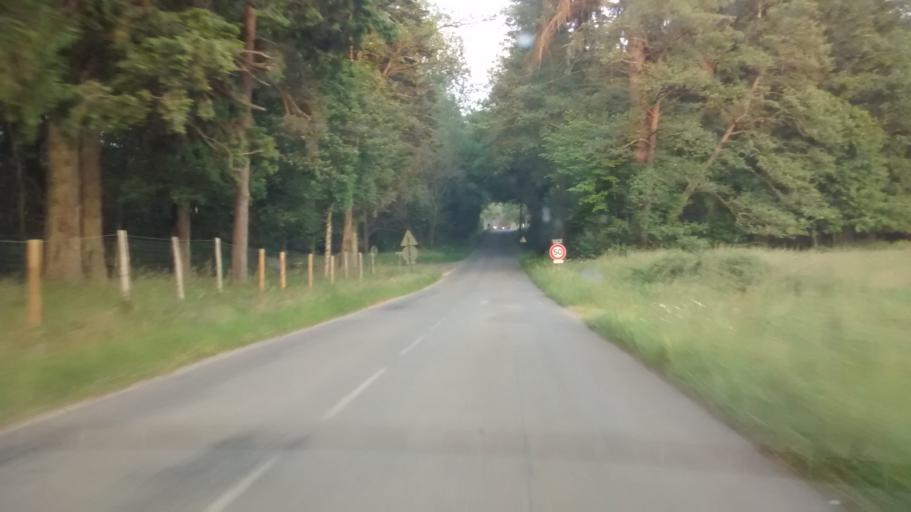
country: FR
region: Brittany
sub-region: Departement d'Ille-et-Vilaine
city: Paimpont
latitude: 47.9961
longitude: -2.1438
